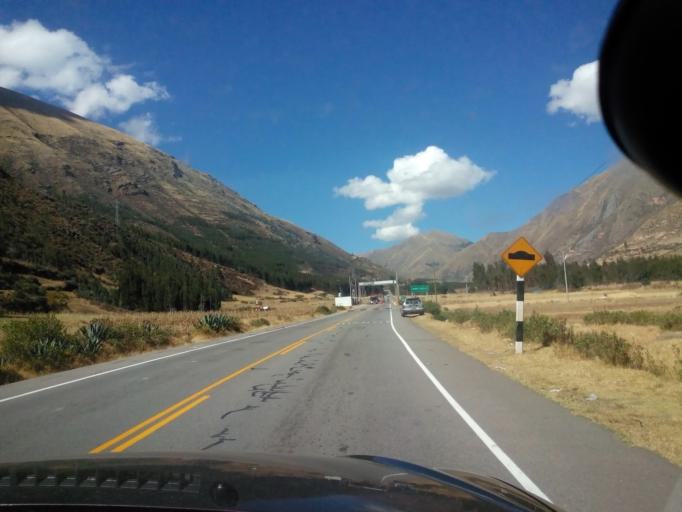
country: PE
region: Cusco
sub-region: Provincia de Quispicanchis
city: Cusipata
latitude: -13.9263
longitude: -71.5052
